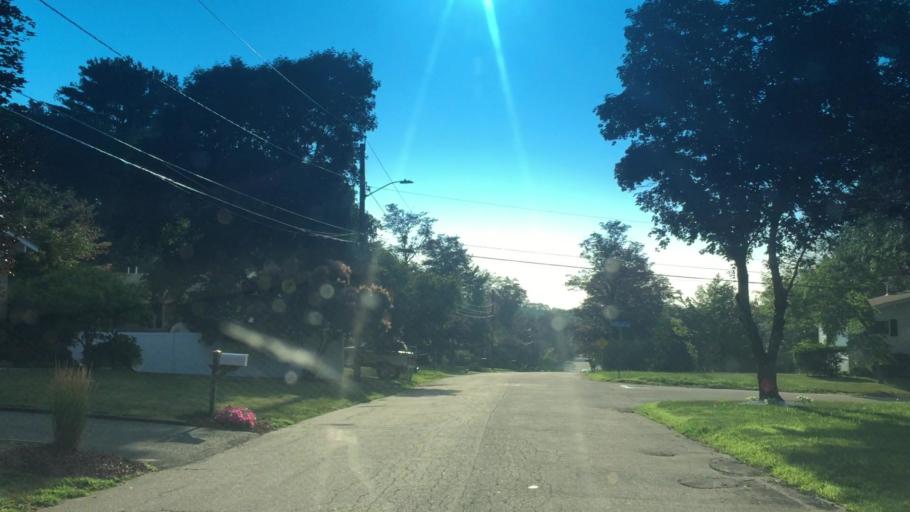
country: US
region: Massachusetts
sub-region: Norfolk County
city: Medway
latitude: 42.1560
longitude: -71.4057
